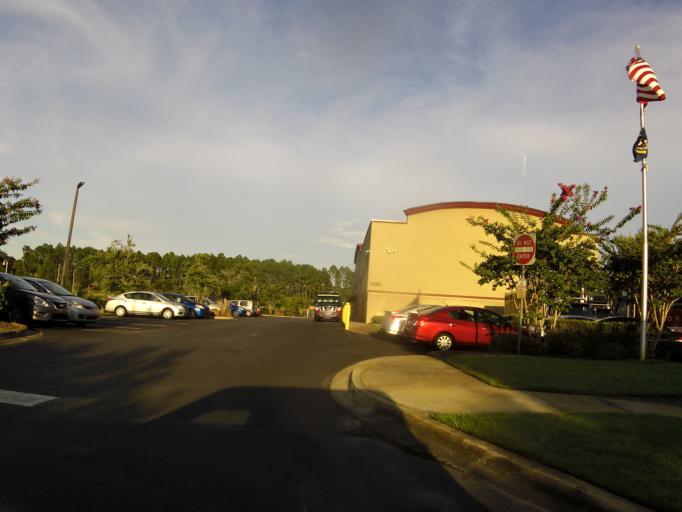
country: US
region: Florida
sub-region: Clay County
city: Orange Park
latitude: 30.2238
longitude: -81.7031
